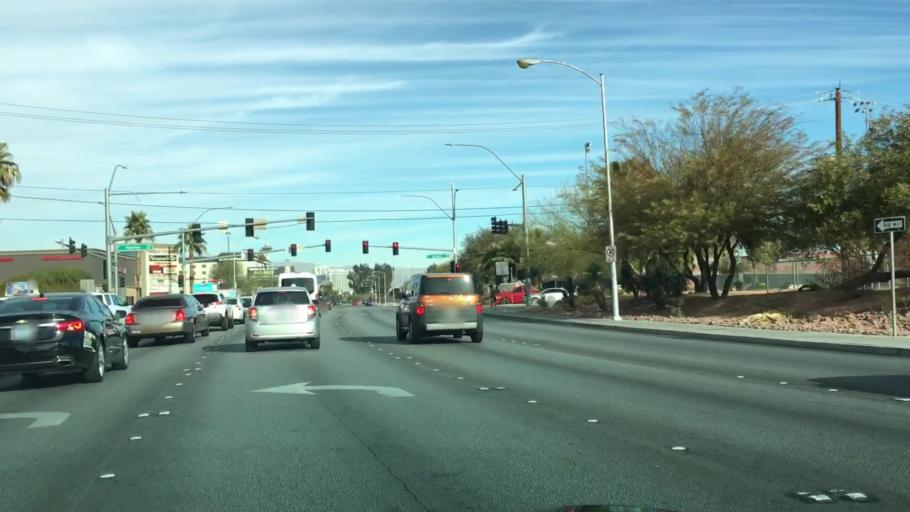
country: US
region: Nevada
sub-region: Clark County
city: Paradise
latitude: 36.1073
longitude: -115.1504
